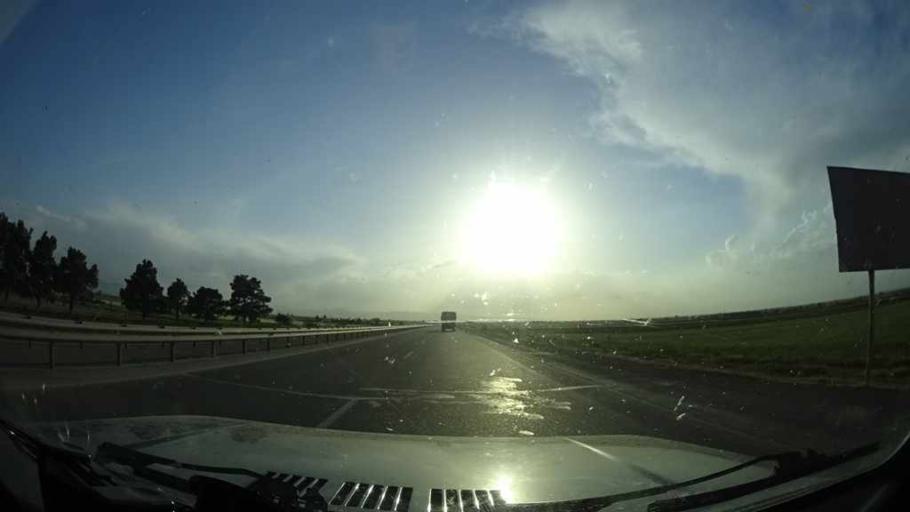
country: AZ
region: Samux
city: Samux
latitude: 40.6896
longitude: 46.5384
